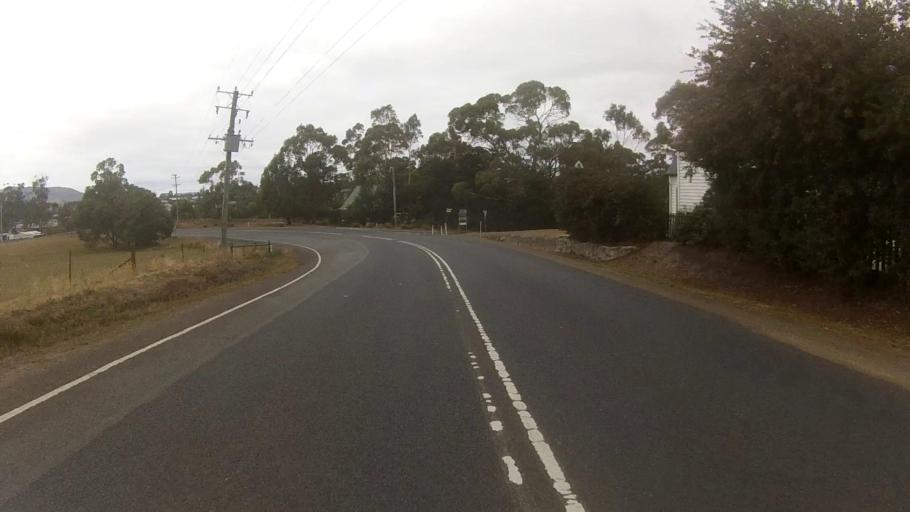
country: AU
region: Tasmania
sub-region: Kingborough
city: Margate
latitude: -43.0220
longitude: 147.2557
